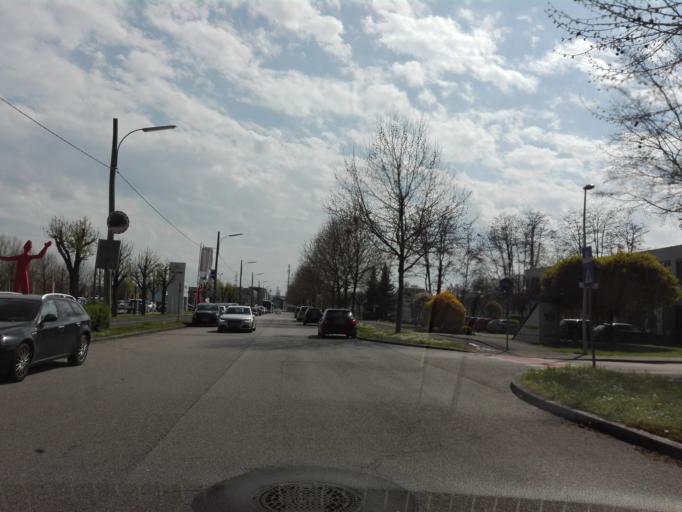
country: AT
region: Upper Austria
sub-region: Politischer Bezirk Linz-Land
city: Ansfelden
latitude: 48.2466
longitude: 14.2938
